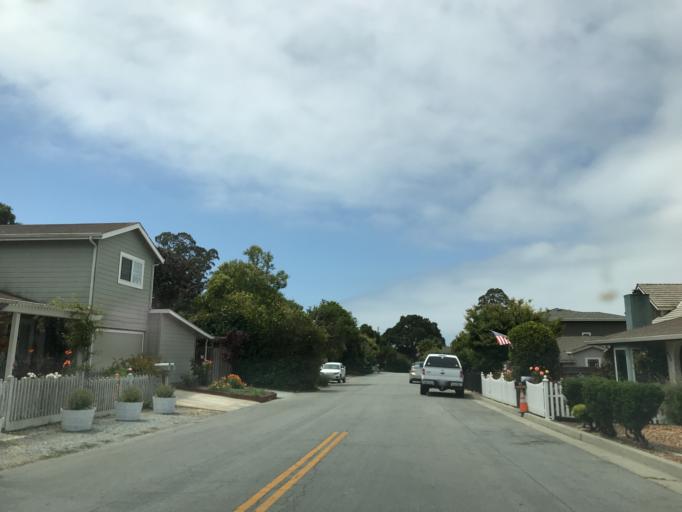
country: US
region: California
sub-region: Santa Cruz County
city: Capitola
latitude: 36.9779
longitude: -121.9482
